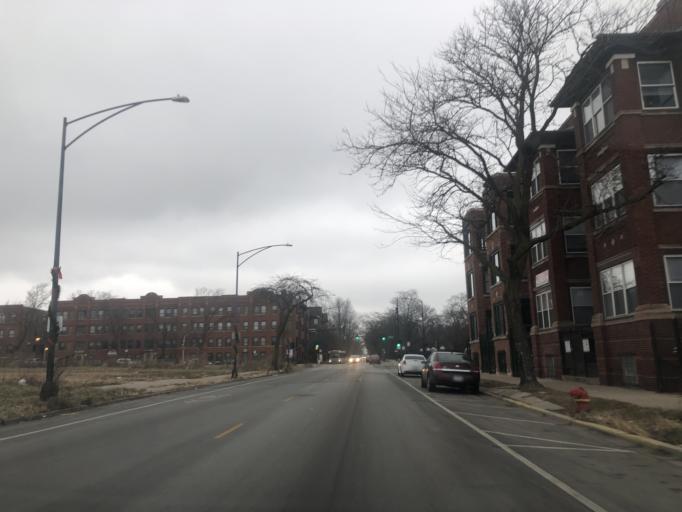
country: US
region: Illinois
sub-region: Cook County
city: Chicago
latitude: 41.7846
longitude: -87.6157
